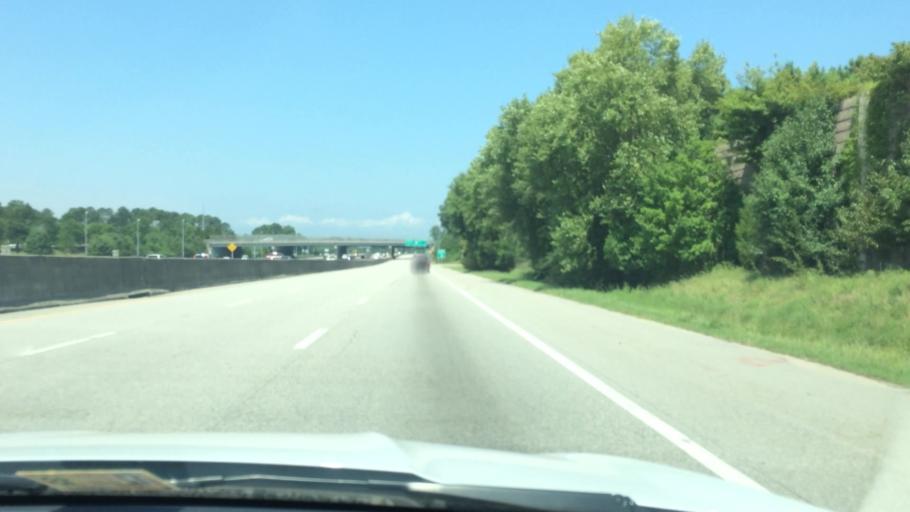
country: US
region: Virginia
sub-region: York County
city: Yorktown
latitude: 37.1161
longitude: -76.4985
